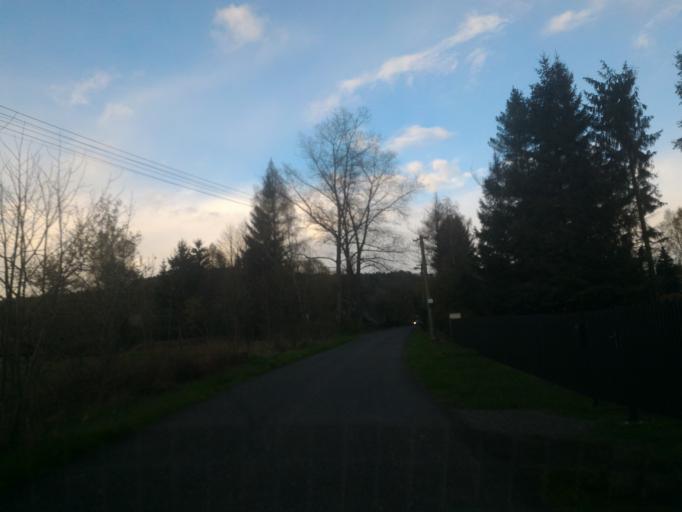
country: CZ
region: Ustecky
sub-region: Okres Decin
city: Chribska
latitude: 50.8902
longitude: 14.4659
